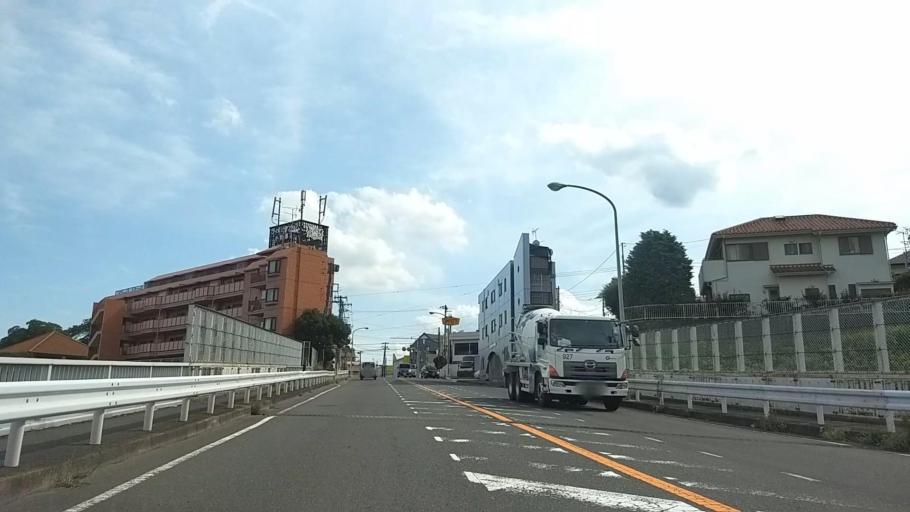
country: JP
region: Kanagawa
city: Yokohama
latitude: 35.5126
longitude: 139.5845
